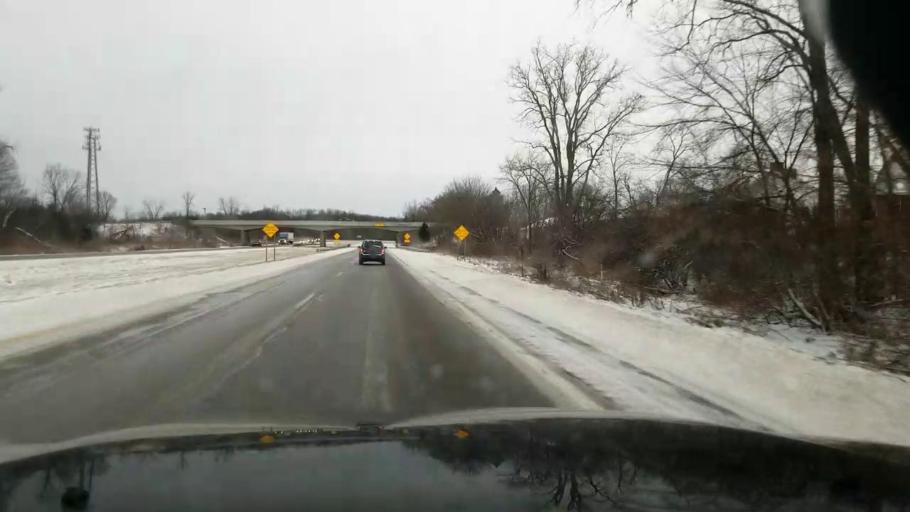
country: US
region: Michigan
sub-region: Jackson County
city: Jackson
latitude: 42.2346
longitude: -84.4753
